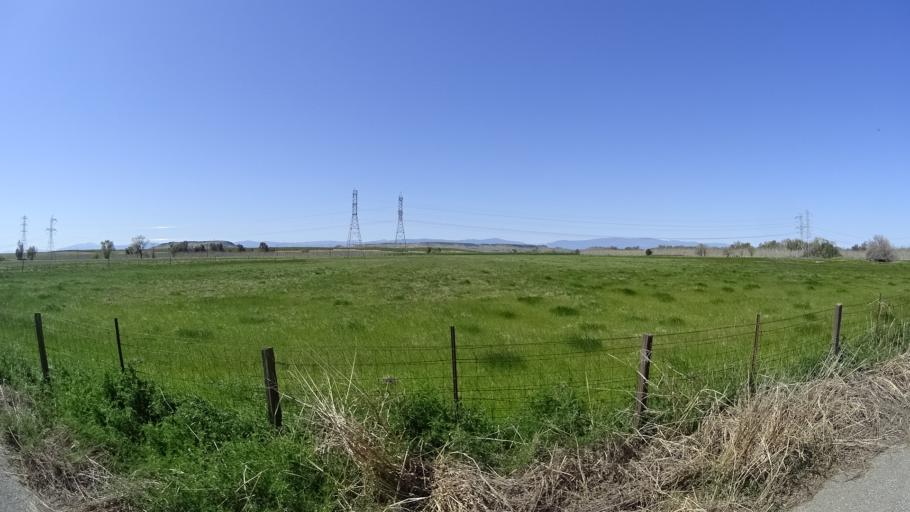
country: US
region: California
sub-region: Glenn County
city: Orland
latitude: 39.7783
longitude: -122.2713
